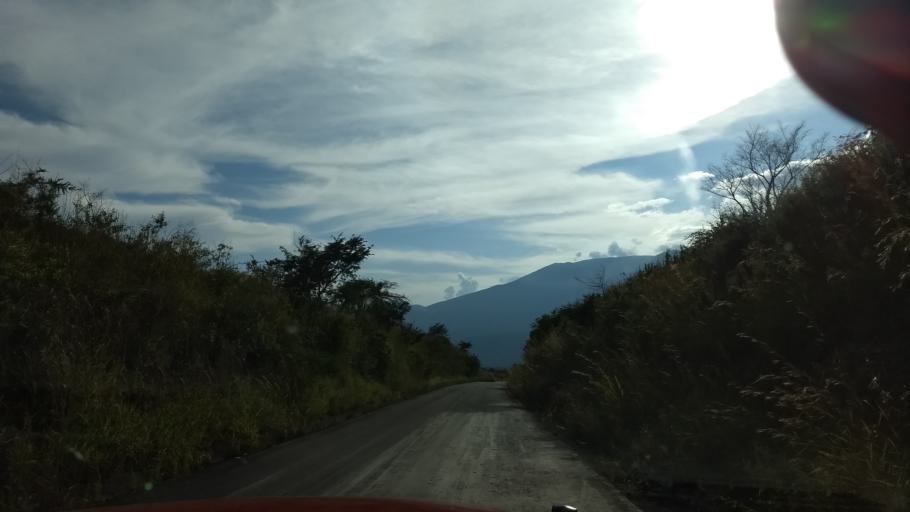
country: MX
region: Colima
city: Suchitlan
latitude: 19.4637
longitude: -103.7851
